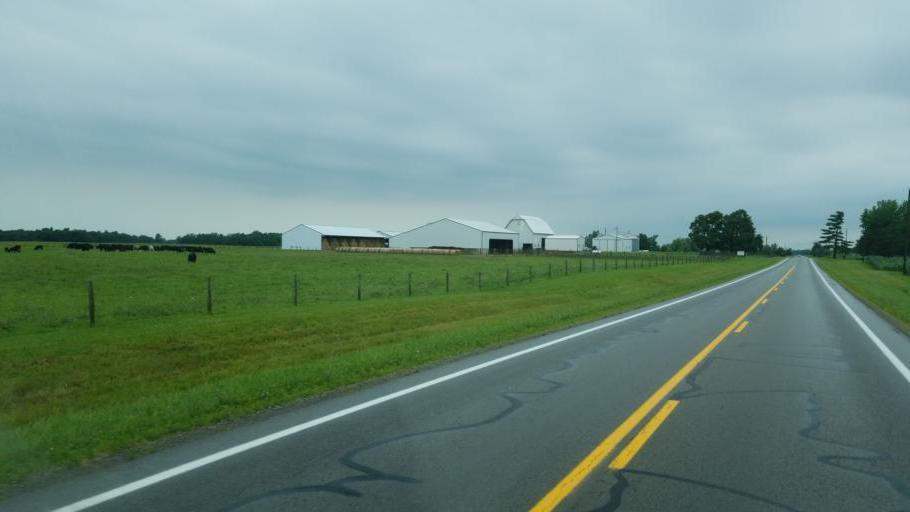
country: US
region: Ohio
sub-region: Hardin County
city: Kenton
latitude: 40.5990
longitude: -83.5940
